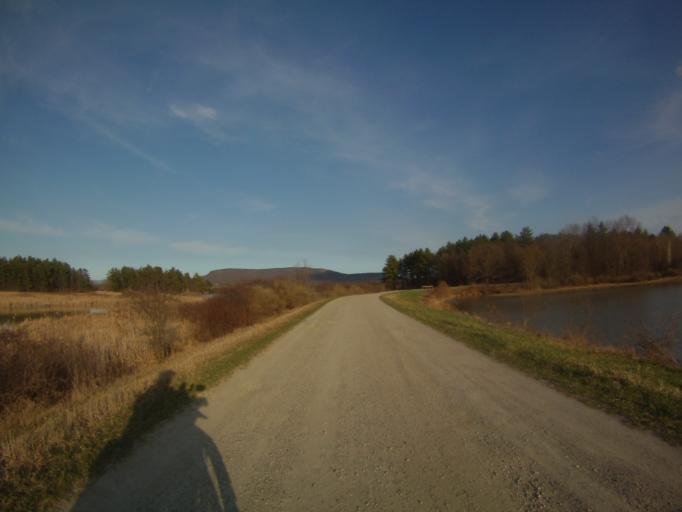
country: US
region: New York
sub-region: Essex County
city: Port Henry
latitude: 44.0742
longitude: -73.3489
